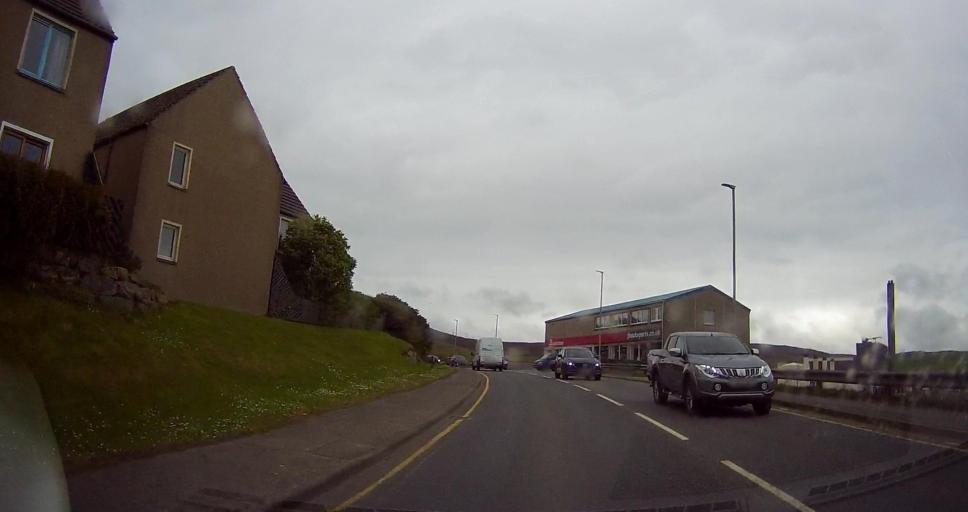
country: GB
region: Scotland
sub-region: Shetland Islands
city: Lerwick
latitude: 60.1640
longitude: -1.1609
